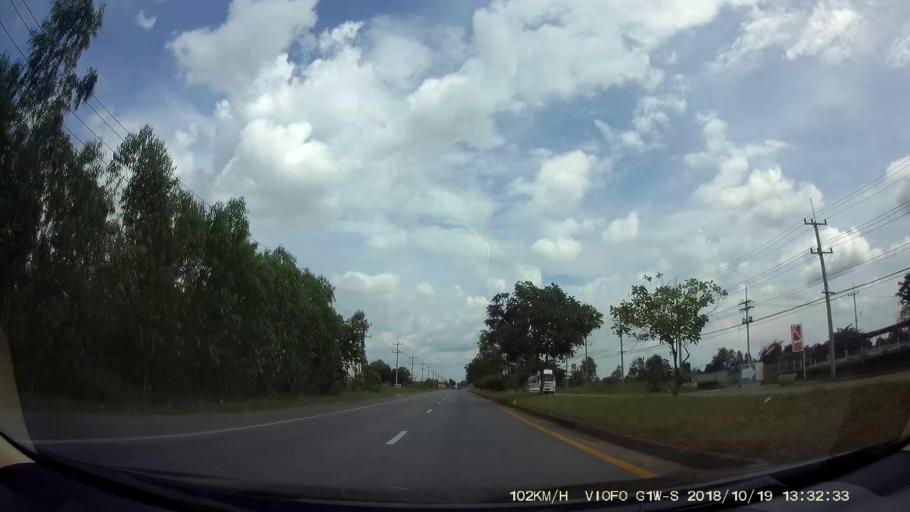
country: TH
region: Chaiyaphum
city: Chatturat
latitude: 15.5777
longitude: 101.8834
